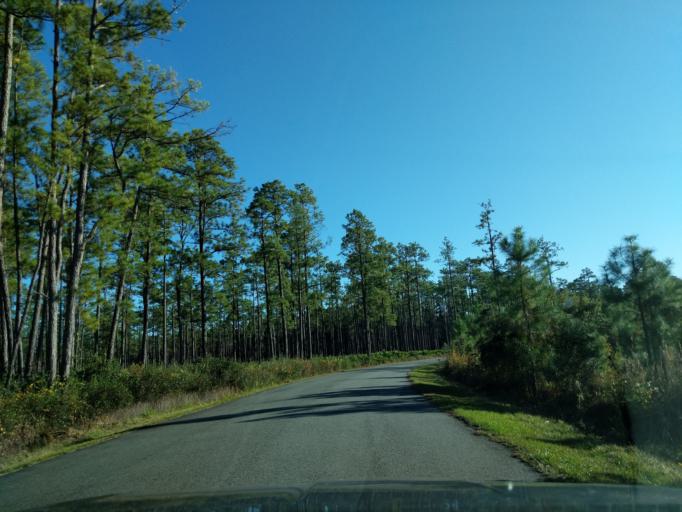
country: US
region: Georgia
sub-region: Charlton County
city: Folkston
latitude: 30.7369
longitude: -82.1363
